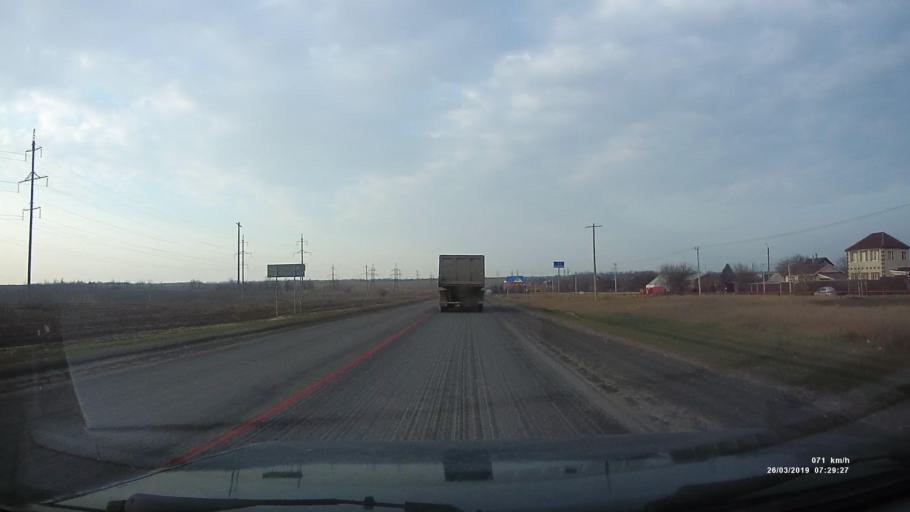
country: RU
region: Rostov
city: Novobessergenovka
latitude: 47.2450
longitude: 38.8163
